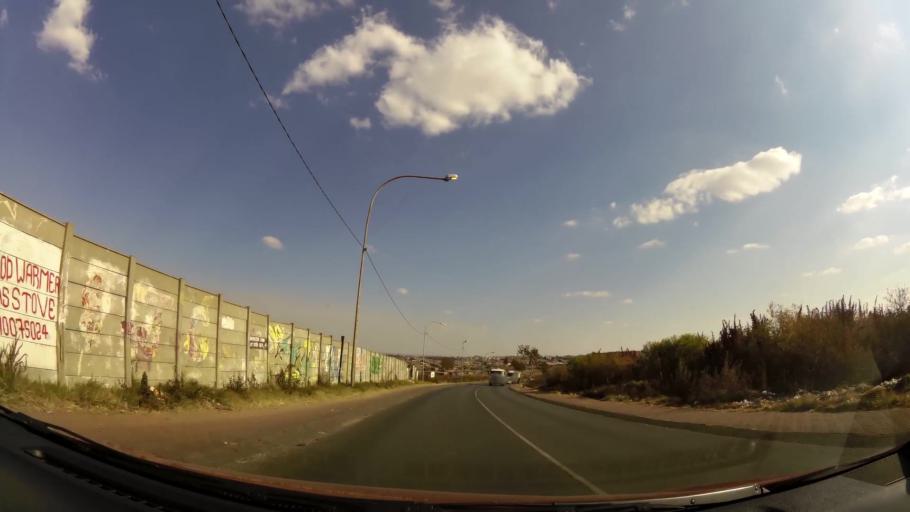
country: ZA
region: Gauteng
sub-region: City of Johannesburg Metropolitan Municipality
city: Soweto
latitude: -26.2236
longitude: 27.8878
